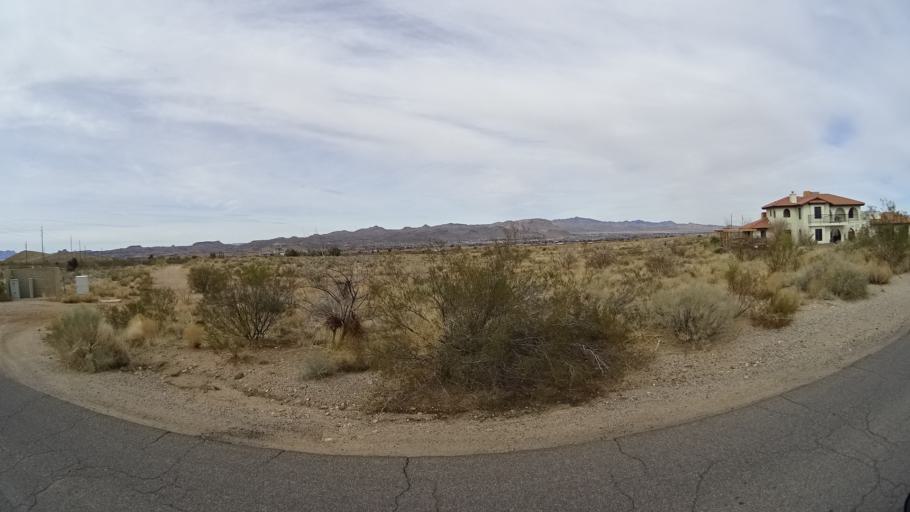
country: US
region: Arizona
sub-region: Mohave County
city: Kingman
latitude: 35.1810
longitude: -113.9939
